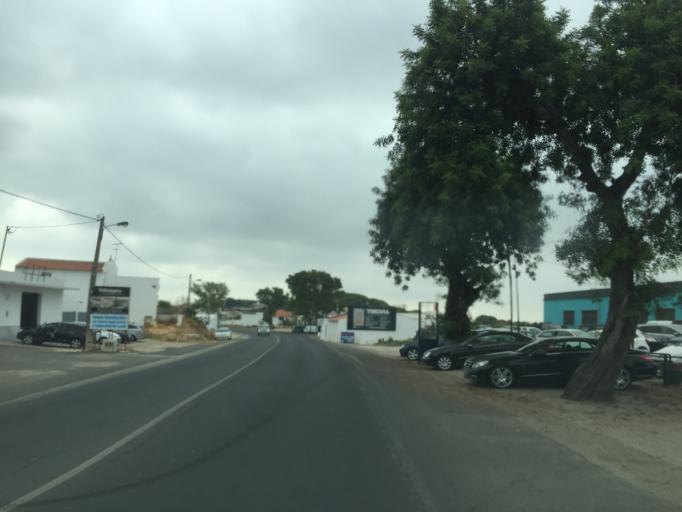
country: PT
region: Faro
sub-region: Faro
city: Santa Barbara de Nexe
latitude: 37.0777
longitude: -7.9900
